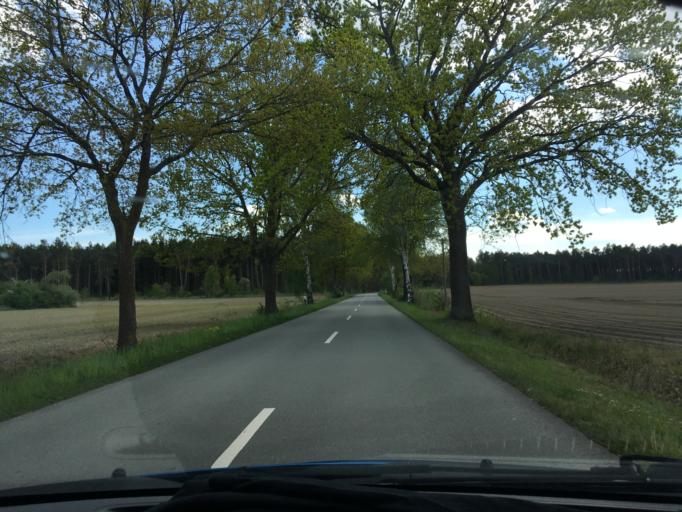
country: DE
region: Lower Saxony
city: Nahrendorf
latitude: 53.1543
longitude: 10.8127
